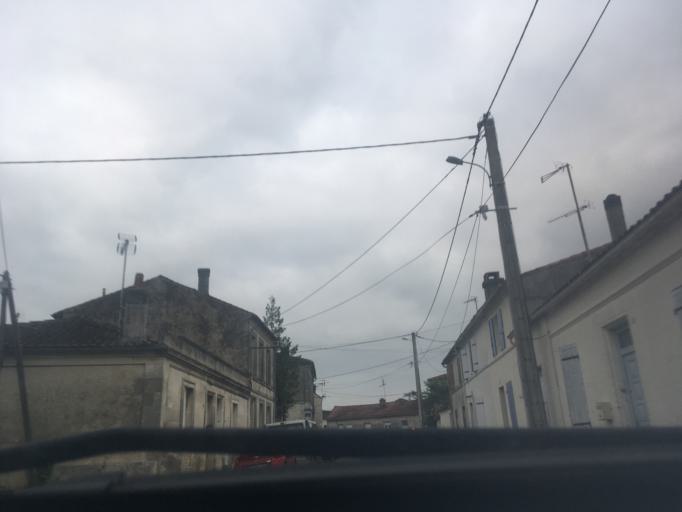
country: FR
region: Poitou-Charentes
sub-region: Departement de la Charente
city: Cognac
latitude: 45.6834
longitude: -0.3296
